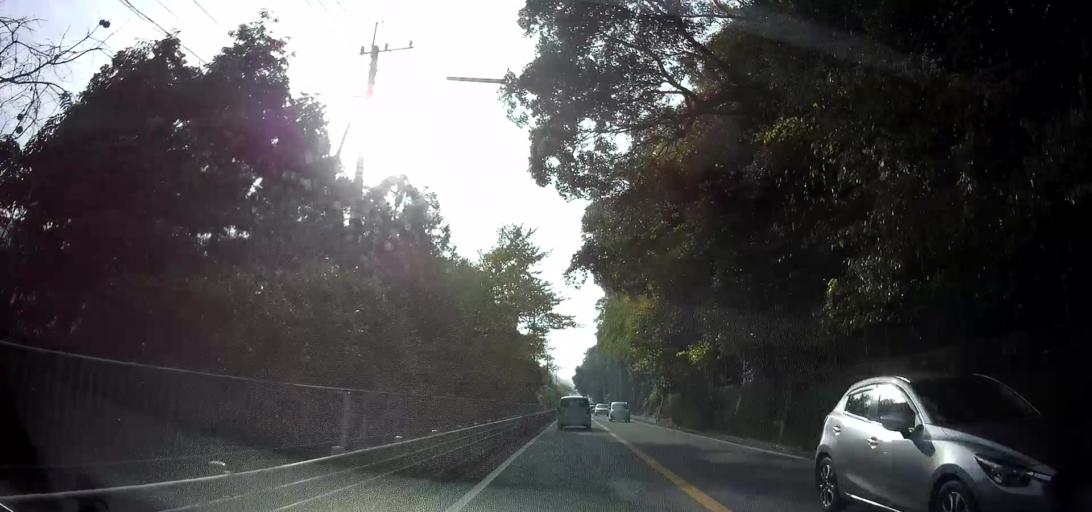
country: JP
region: Nagasaki
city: Shimabara
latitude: 32.7741
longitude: 130.2135
